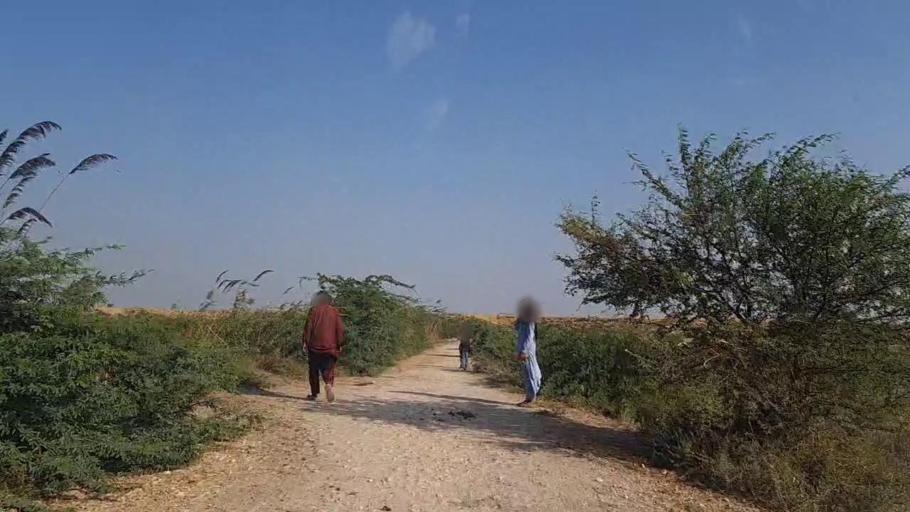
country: PK
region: Sindh
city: Thatta
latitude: 24.7389
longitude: 67.9693
